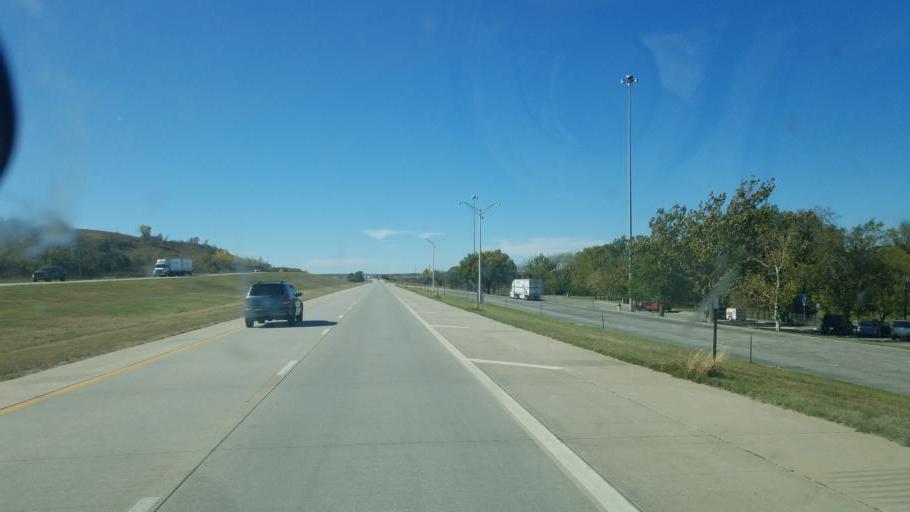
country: US
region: Kansas
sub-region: Riley County
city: Ogden
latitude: 39.0664
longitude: -96.6213
